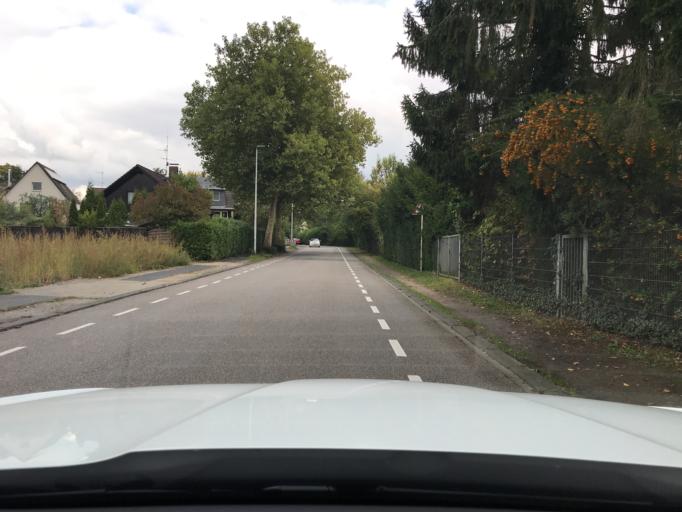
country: DE
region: North Rhine-Westphalia
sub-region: Regierungsbezirk Dusseldorf
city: Muelheim (Ruhr)
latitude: 51.4189
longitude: 6.8639
